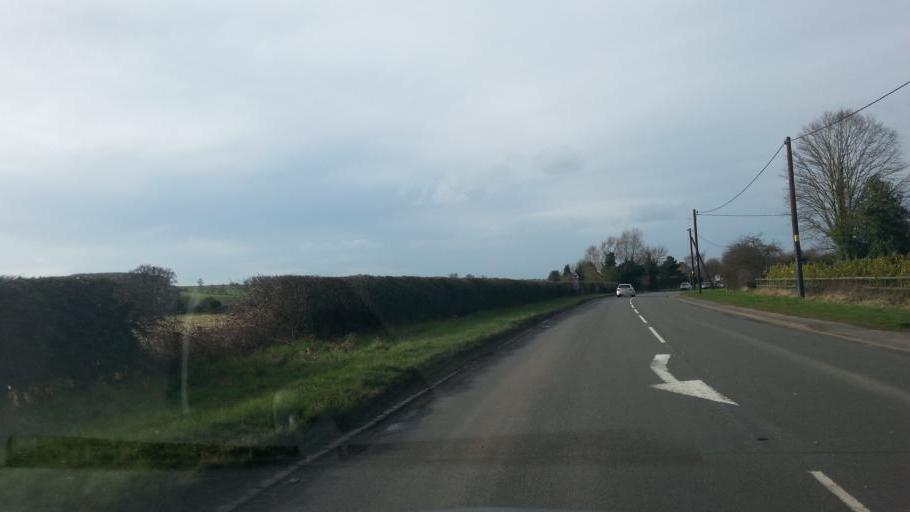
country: GB
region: England
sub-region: Staffordshire
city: Colwich
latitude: 52.8286
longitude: -2.0216
